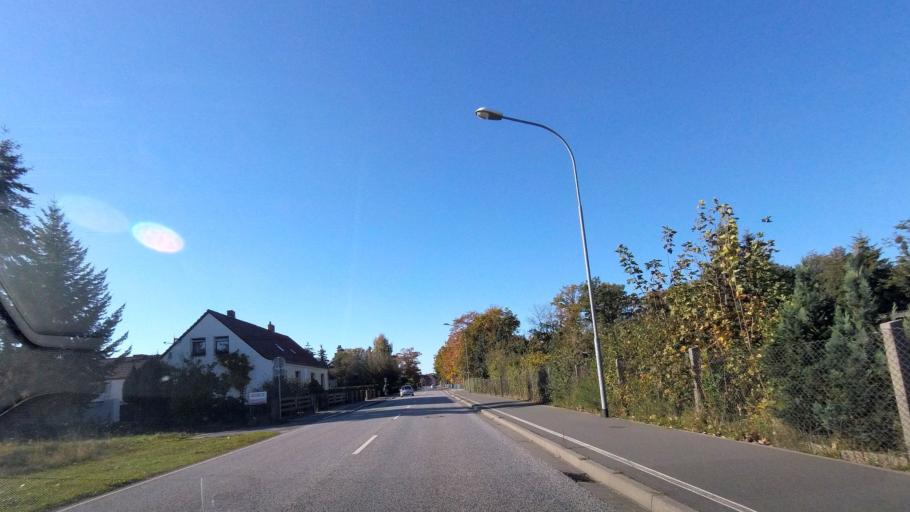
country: DE
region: Saxony-Anhalt
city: Muhlanger
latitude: 51.8511
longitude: 12.7542
